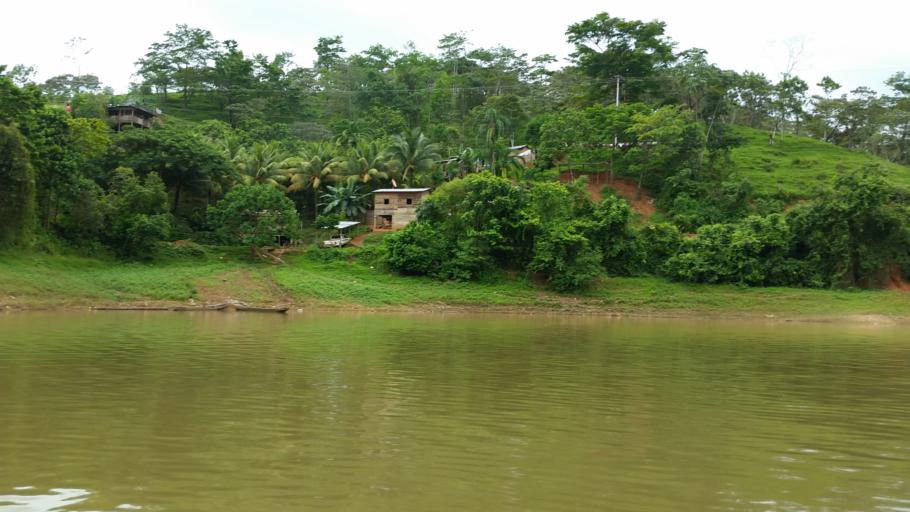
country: NI
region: Atlantico Norte (RAAN)
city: Bonanza
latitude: 13.9769
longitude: -84.6992
